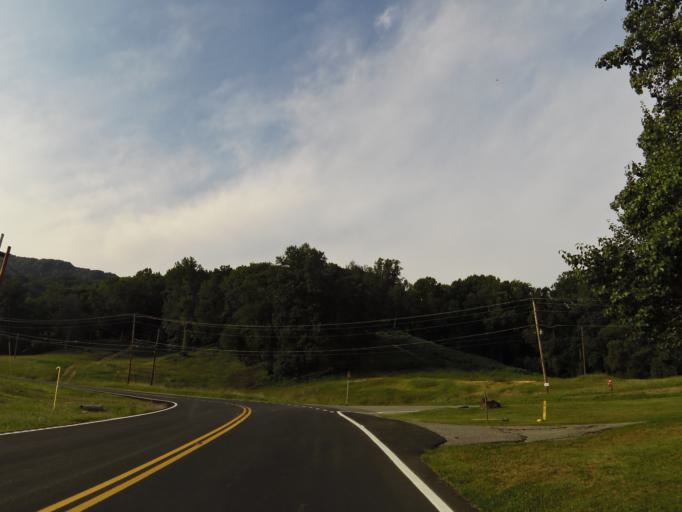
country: US
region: Tennessee
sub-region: Morgan County
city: Coalfield
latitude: 36.1023
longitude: -84.4470
